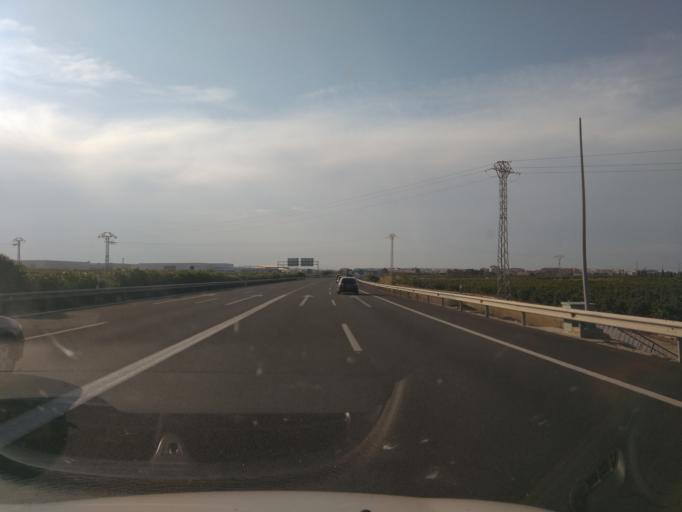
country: ES
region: Valencia
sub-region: Provincia de Valencia
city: Alcasser
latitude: 39.3526
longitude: -0.4338
